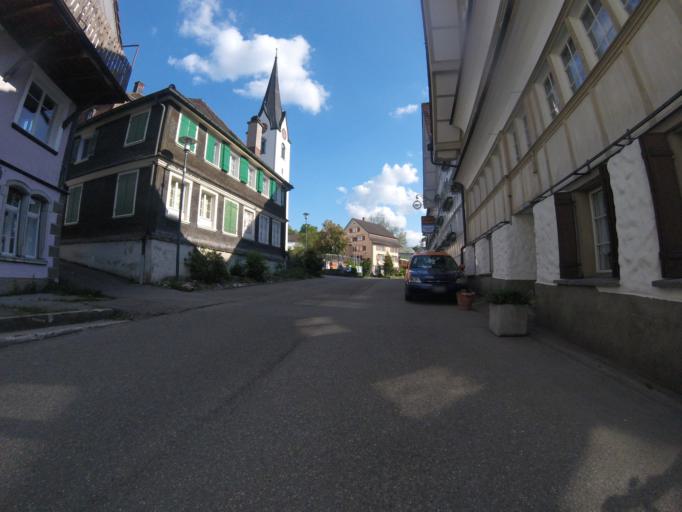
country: CH
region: Saint Gallen
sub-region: Wahlkreis Toggenburg
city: Mogelsberg
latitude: 47.3627
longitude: 9.1357
